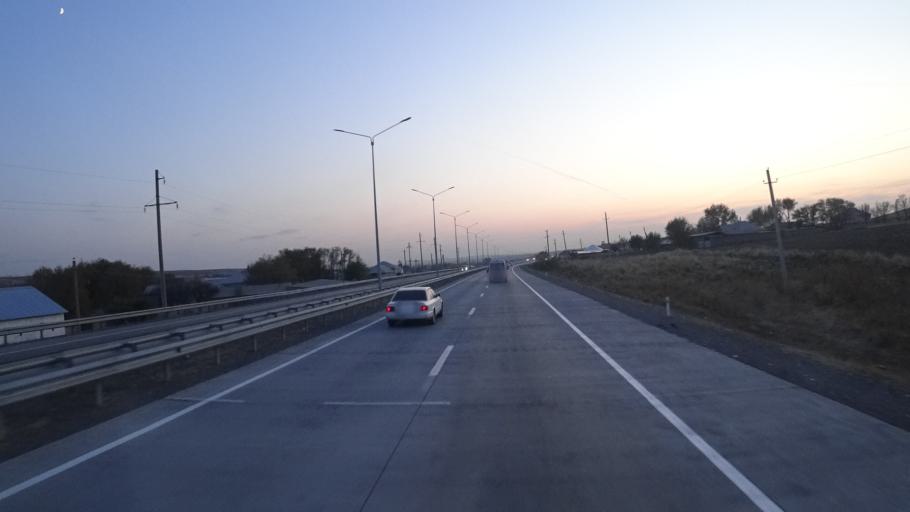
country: KZ
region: Ongtustik Qazaqstan
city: Qazyqurt
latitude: 41.8814
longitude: 69.4373
